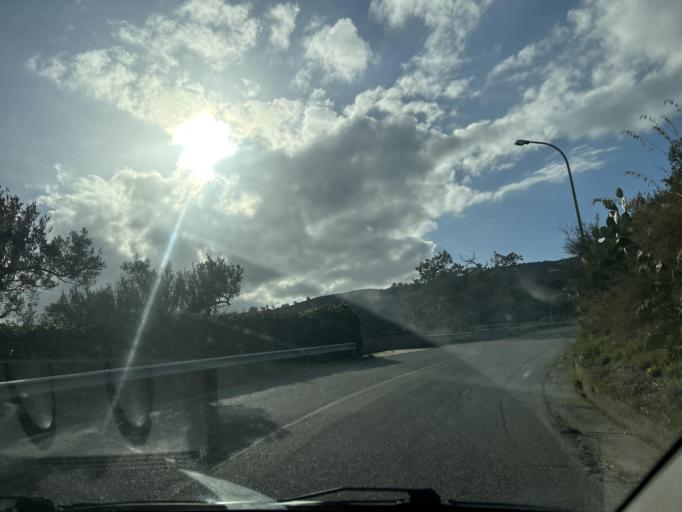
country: IT
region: Calabria
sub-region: Provincia di Catanzaro
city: Montepaone
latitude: 38.7199
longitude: 16.5045
